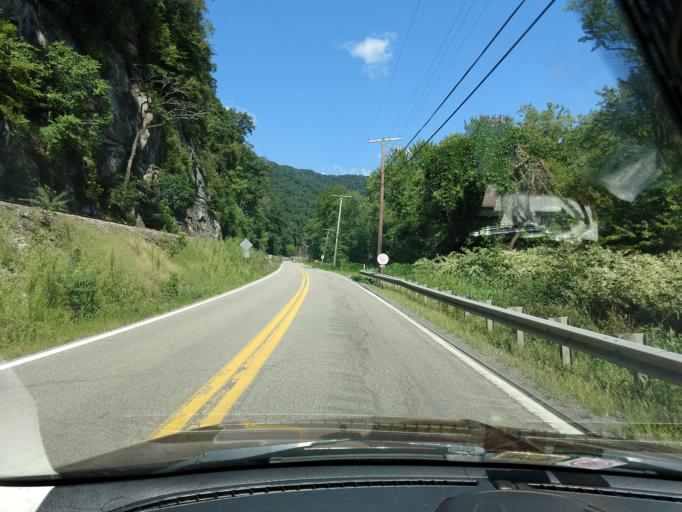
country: US
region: West Virginia
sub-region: Fayette County
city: Ansted
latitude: 38.1438
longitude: -81.2122
